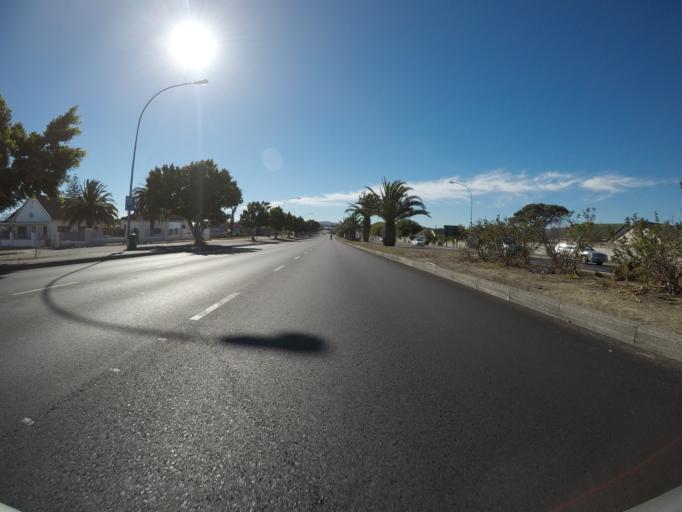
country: ZA
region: Western Cape
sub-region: City of Cape Town
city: Kraaifontein
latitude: -33.9173
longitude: 18.6728
